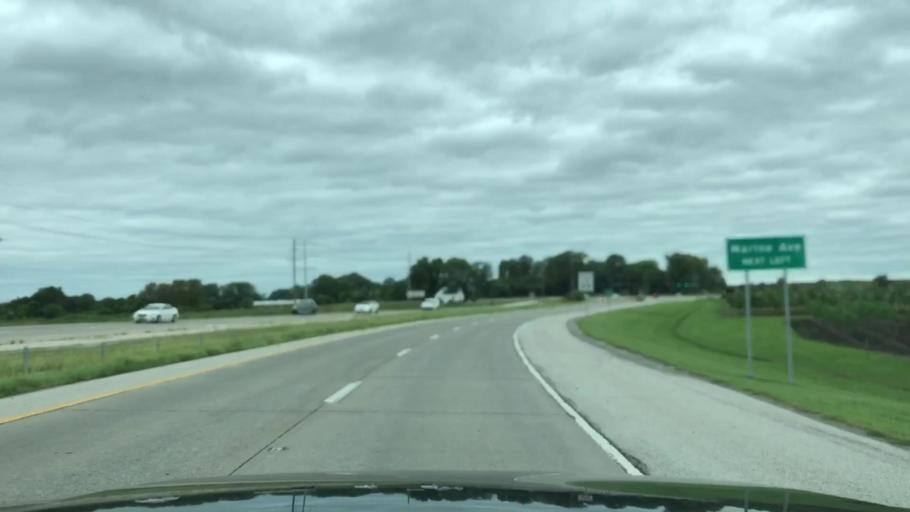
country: US
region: Missouri
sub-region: Saint Charles County
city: Saint Charles
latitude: 38.7317
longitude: -90.4829
